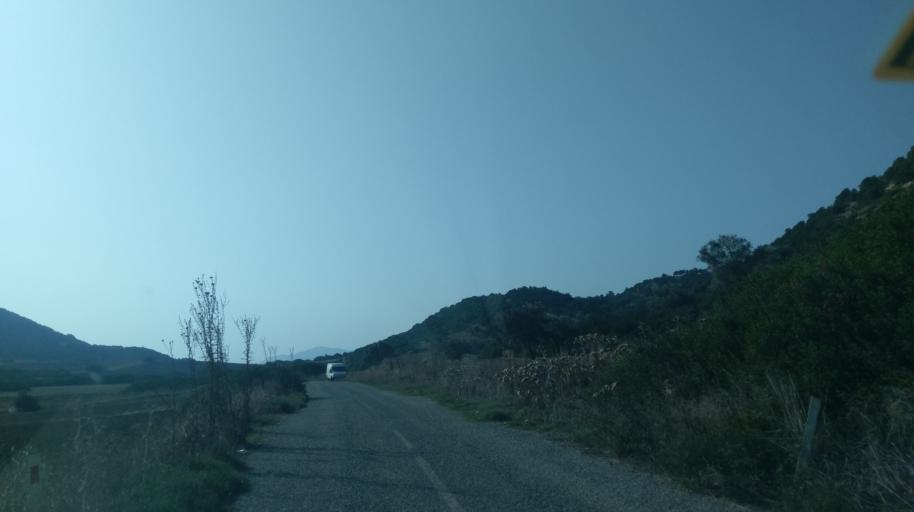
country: CY
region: Ammochostos
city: Rizokarpaso
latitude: 35.5531
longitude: 34.3636
